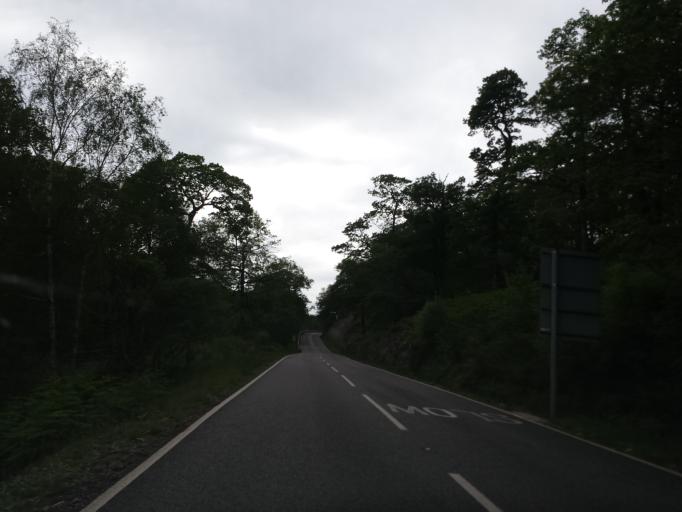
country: GB
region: Scotland
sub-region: Argyll and Bute
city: Isle Of Mull
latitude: 56.9016
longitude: -5.7559
